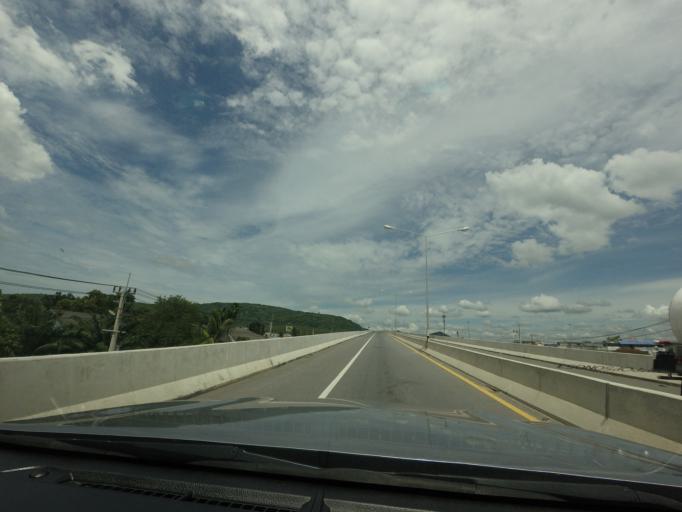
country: TH
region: Songkhla
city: Songkhla
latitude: 7.1333
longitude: 100.5767
